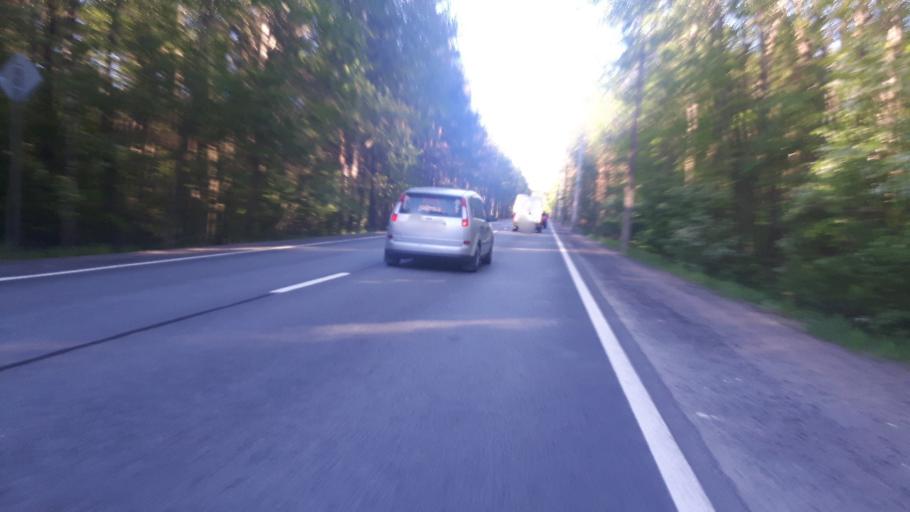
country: RU
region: Leningrad
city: Molodezhnoye
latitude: 60.1765
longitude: 29.4434
